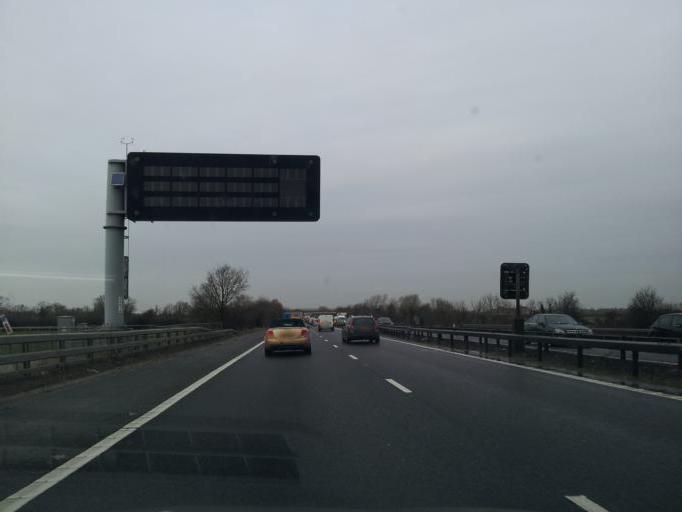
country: GB
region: England
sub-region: Cambridgeshire
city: Barton
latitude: 52.1969
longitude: 0.0744
